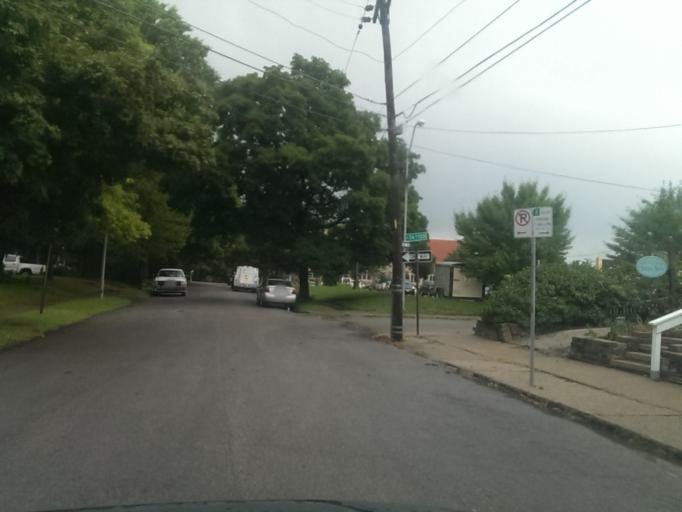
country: US
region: Kansas
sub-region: Johnson County
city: Mission Hills
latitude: 38.9930
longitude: -94.5954
